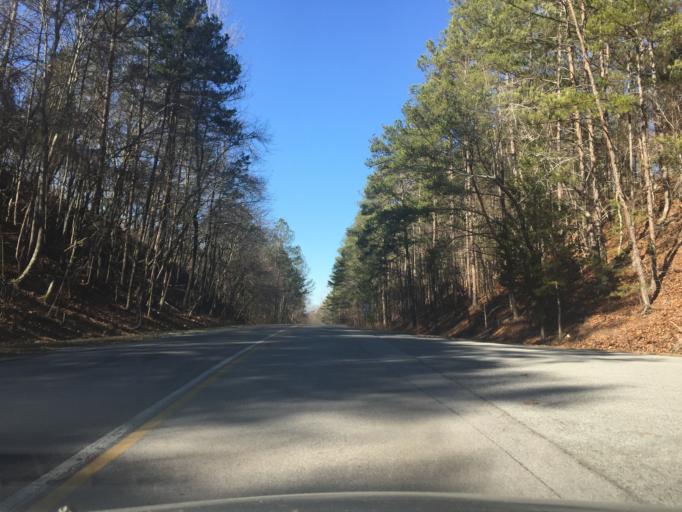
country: US
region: Tennessee
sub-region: Hamilton County
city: Harrison
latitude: 35.0862
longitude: -85.1190
